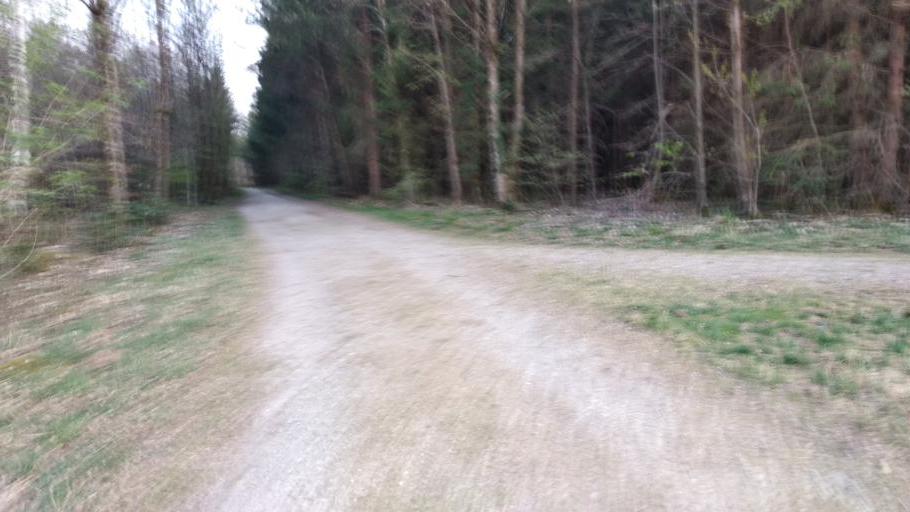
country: DE
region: Bavaria
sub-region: Upper Bavaria
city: Haar
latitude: 48.1015
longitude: 11.7445
